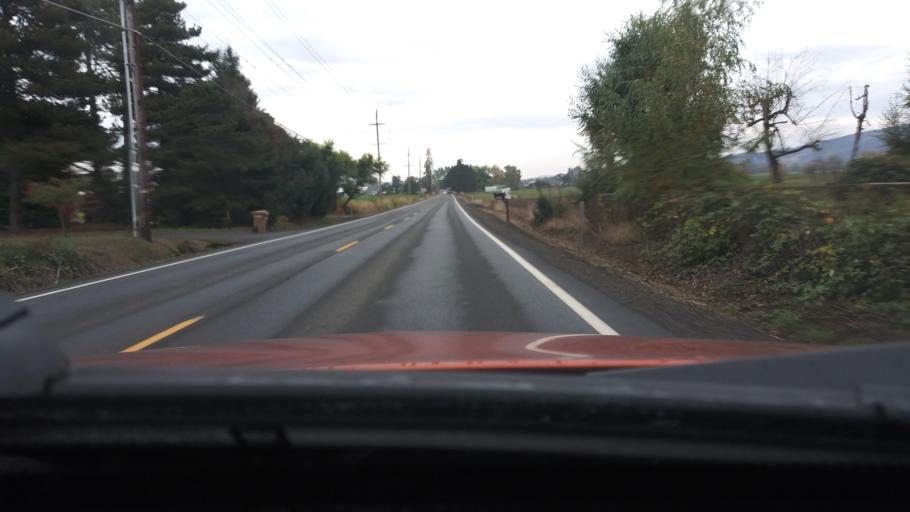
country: US
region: Oregon
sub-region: Washington County
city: Banks
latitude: 45.5924
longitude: -123.1145
